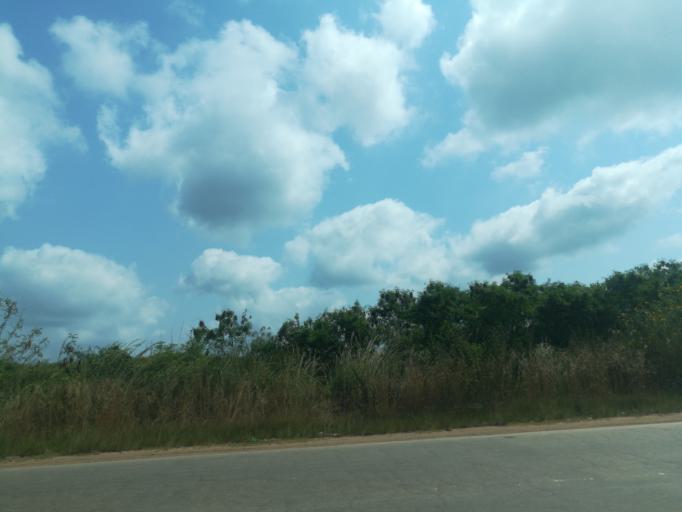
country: NG
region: Oyo
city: Moniya
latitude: 7.5878
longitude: 3.9140
